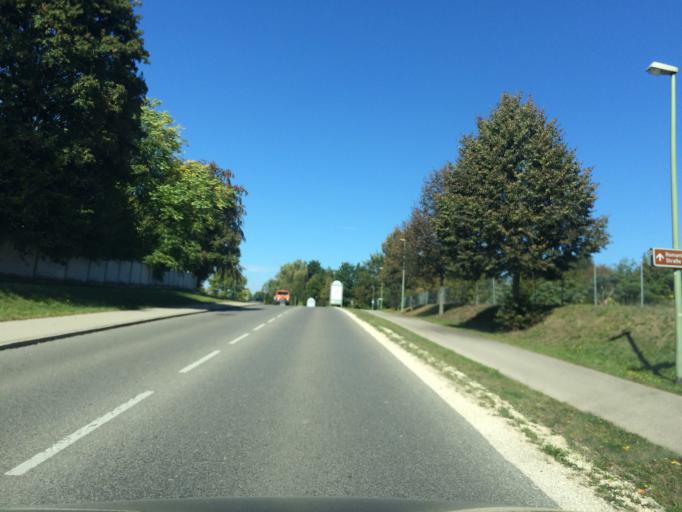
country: DE
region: Bavaria
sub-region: Swabia
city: Friedberg
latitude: 48.3476
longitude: 10.9936
